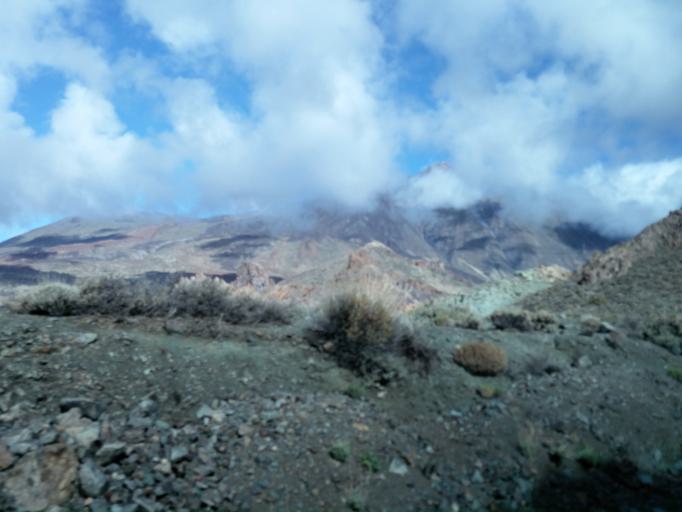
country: ES
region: Canary Islands
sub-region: Provincia de Santa Cruz de Tenerife
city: Vilaflor
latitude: 28.2144
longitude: -16.6275
